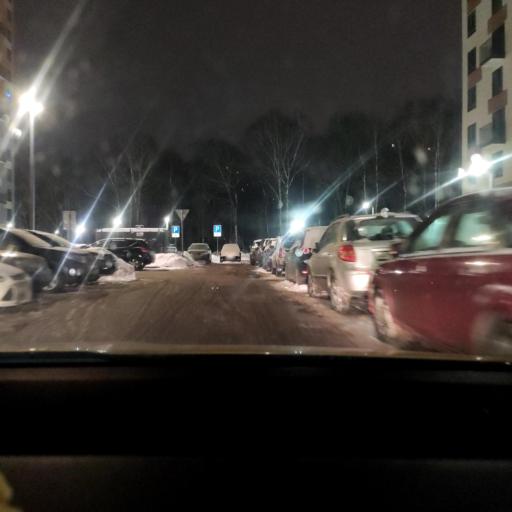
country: RU
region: Moskovskaya
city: Pavshino
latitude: 55.8423
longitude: 37.3464
